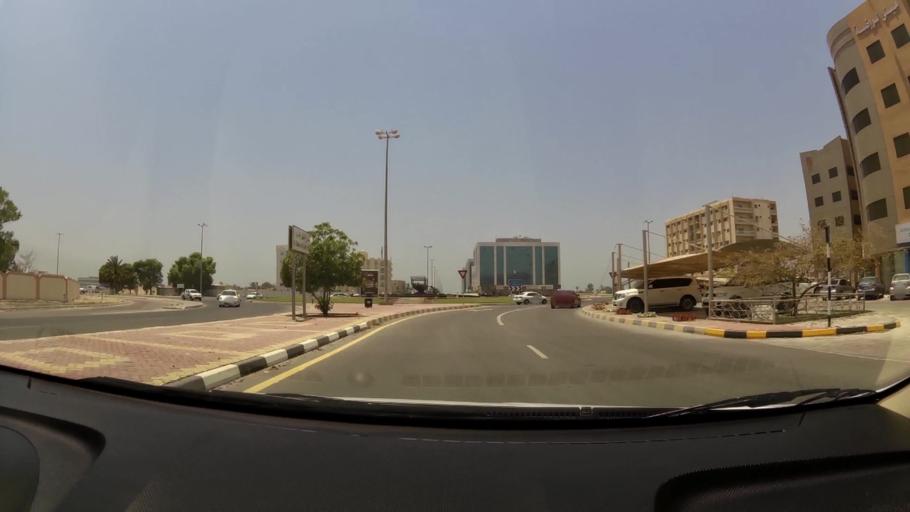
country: AE
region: Umm al Qaywayn
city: Umm al Qaywayn
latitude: 25.5753
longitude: 55.5601
